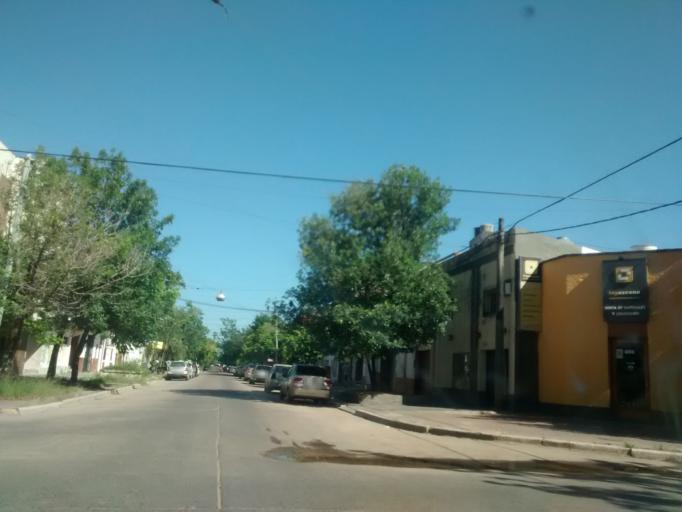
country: AR
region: Chaco
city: Resistencia
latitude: -27.4606
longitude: -58.9864
